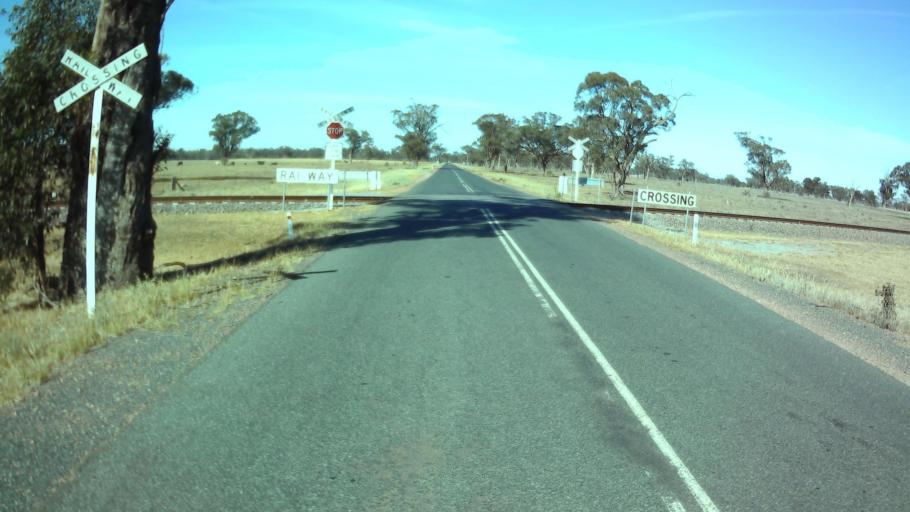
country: AU
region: New South Wales
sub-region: Weddin
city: Grenfell
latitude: -34.1065
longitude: 147.8624
